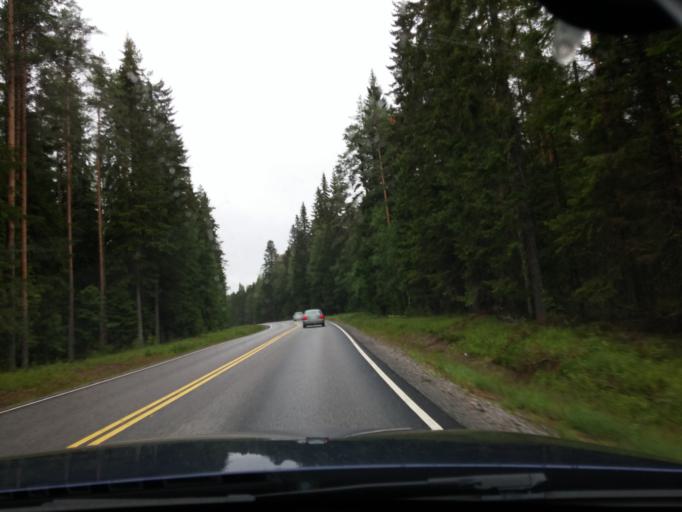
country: FI
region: Central Finland
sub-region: Saarijaervi-Viitasaari
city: Pylkoenmaeki
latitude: 62.5572
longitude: 24.6277
